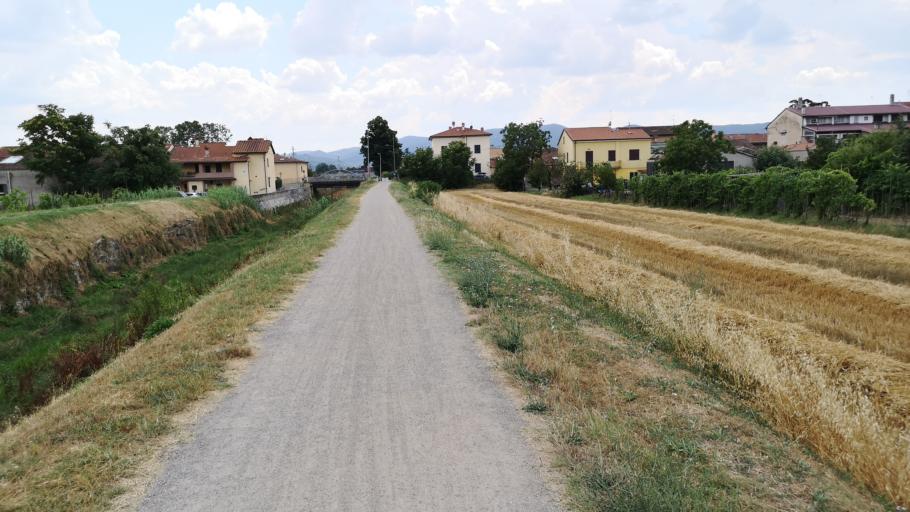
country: IT
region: Tuscany
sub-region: Provincia di Prato
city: Prato
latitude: 43.8758
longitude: 11.0451
